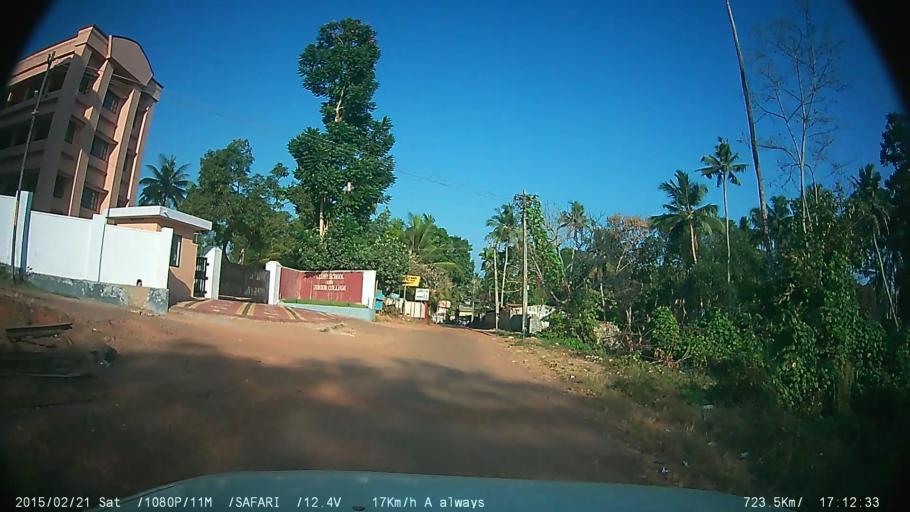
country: IN
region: Kerala
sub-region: Kottayam
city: Changanacheri
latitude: 9.4483
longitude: 76.5503
